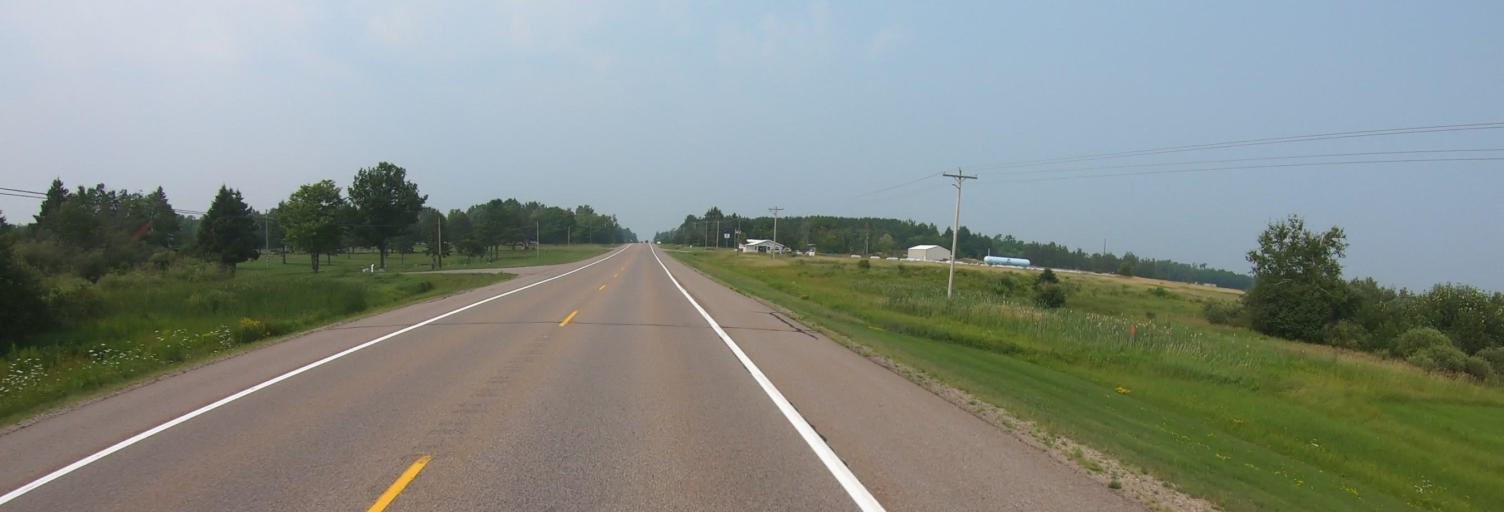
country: US
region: Michigan
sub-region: Chippewa County
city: Sault Ste. Marie
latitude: 46.2815
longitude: -84.3635
